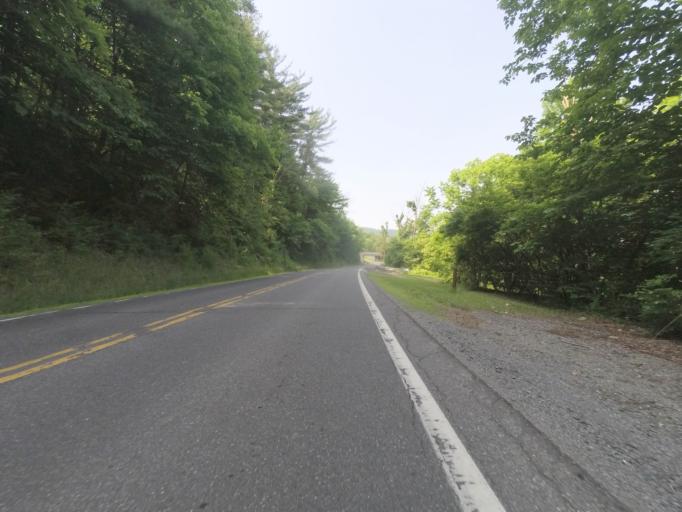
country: US
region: Pennsylvania
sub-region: Centre County
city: Milesburg
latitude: 40.9562
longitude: -77.7491
